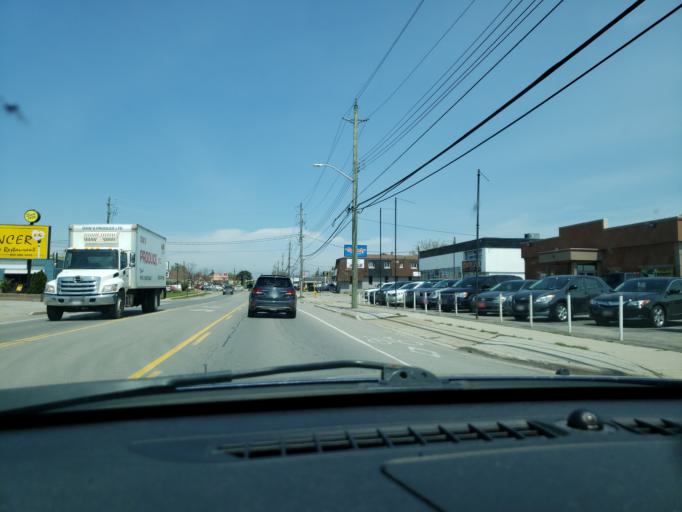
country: CA
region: Ontario
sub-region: Regional Municipality of Niagara
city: St. Catharines
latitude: 43.1527
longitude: -79.2143
